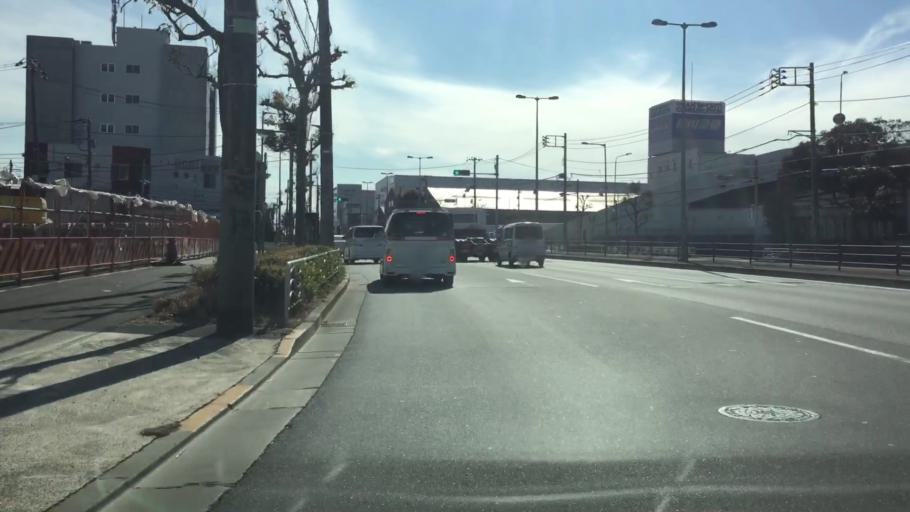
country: JP
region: Tokyo
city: Urayasu
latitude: 35.6391
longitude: 139.8232
